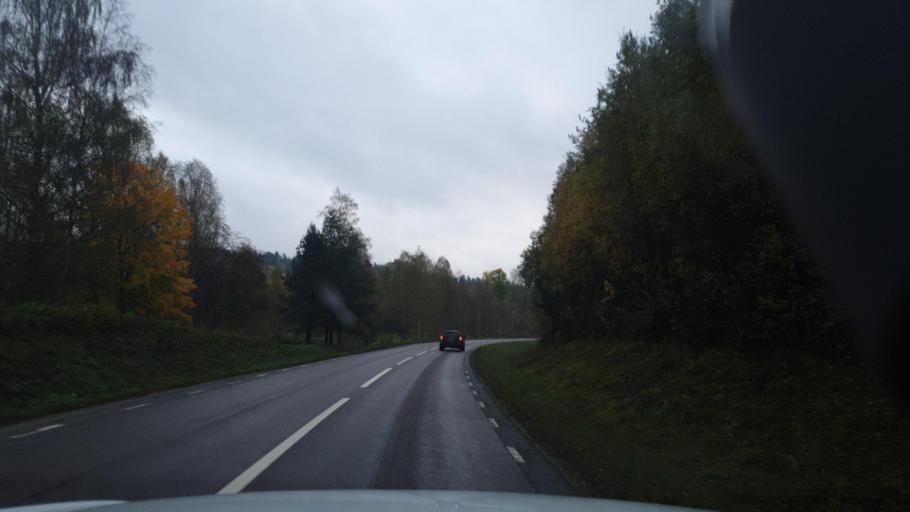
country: SE
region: Vaermland
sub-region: Arvika Kommun
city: Arvika
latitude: 59.6465
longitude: 12.7759
